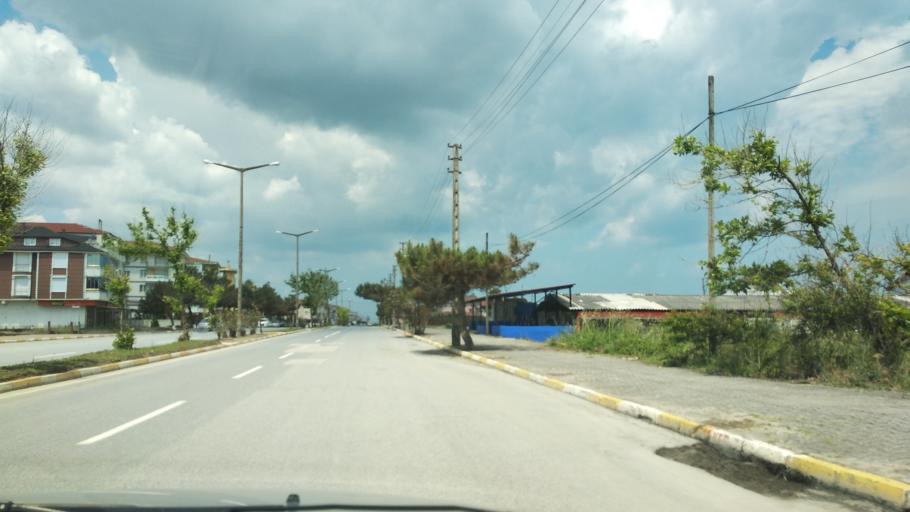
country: TR
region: Sakarya
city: Karasu
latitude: 41.1124
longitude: 30.6865
